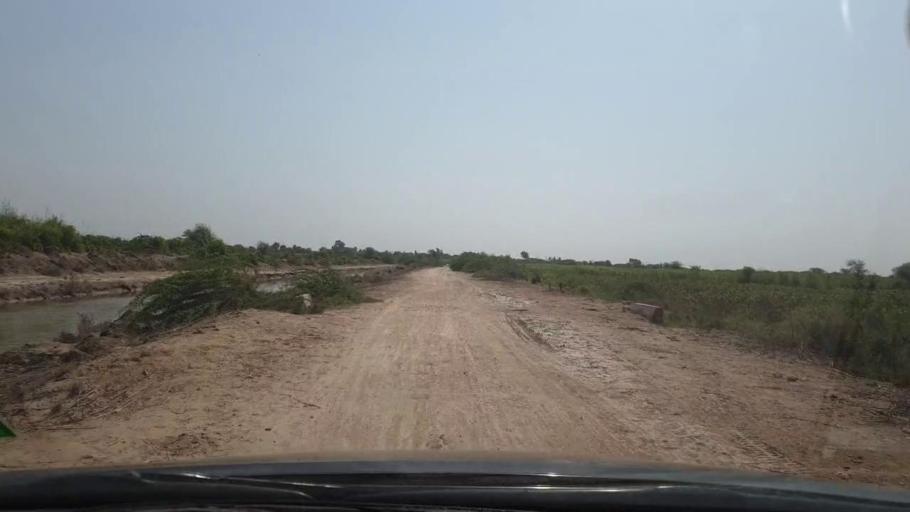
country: PK
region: Sindh
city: Tando Bago
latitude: 24.7877
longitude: 69.1195
